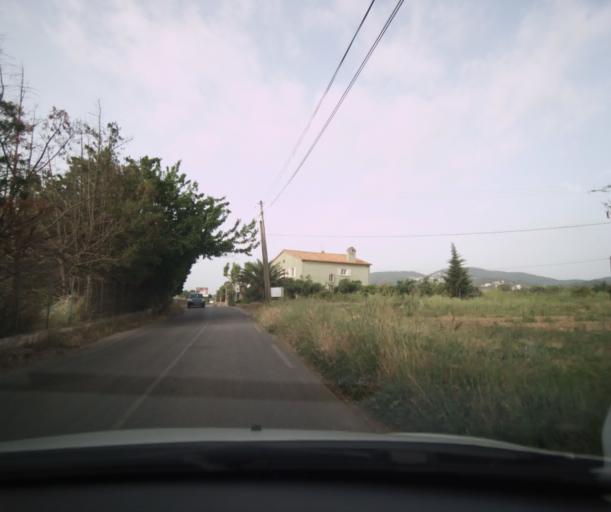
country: FR
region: Provence-Alpes-Cote d'Azur
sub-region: Departement du Var
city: Hyeres
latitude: 43.1118
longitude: 6.1439
